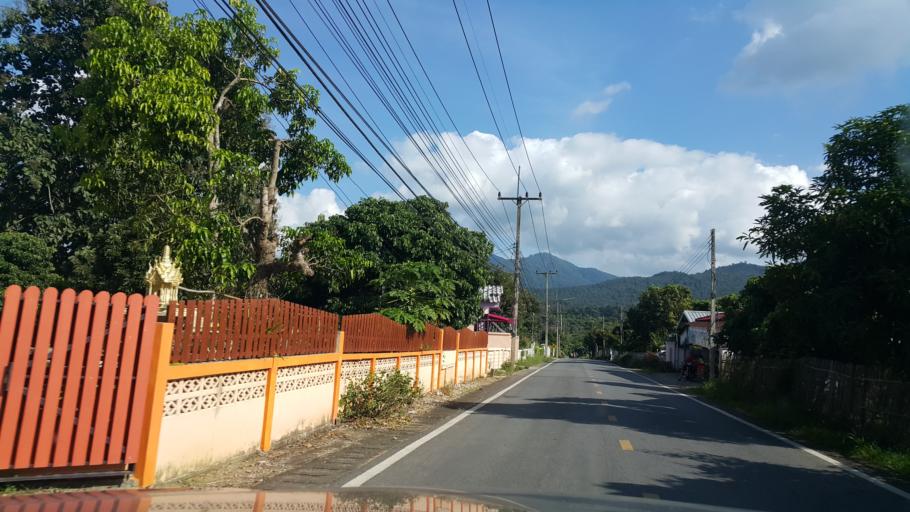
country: TH
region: Lamphun
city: Mae Tha
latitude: 18.5279
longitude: 99.2317
